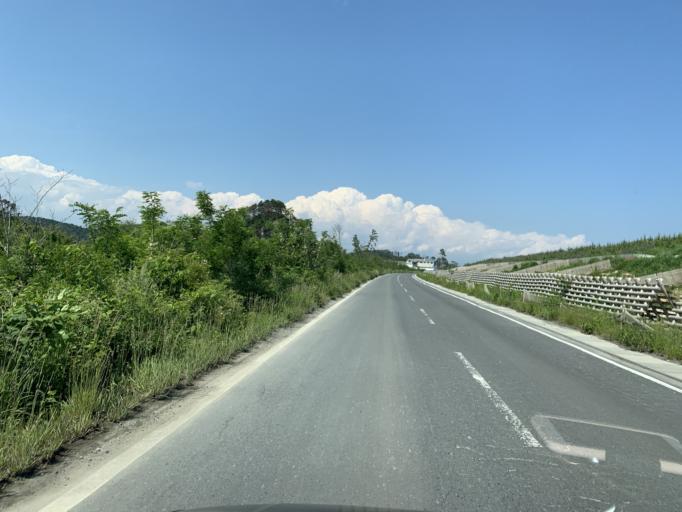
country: JP
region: Miyagi
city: Yamoto
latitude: 38.3671
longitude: 141.1589
